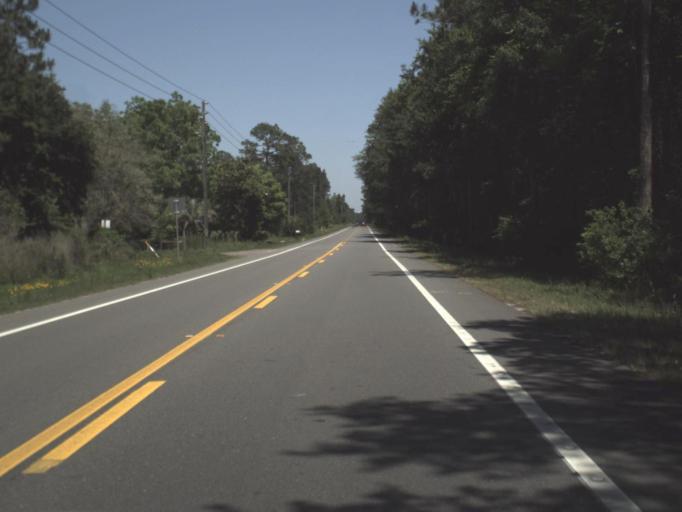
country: US
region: Florida
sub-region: Baker County
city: Macclenny
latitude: 30.2913
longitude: -82.0670
